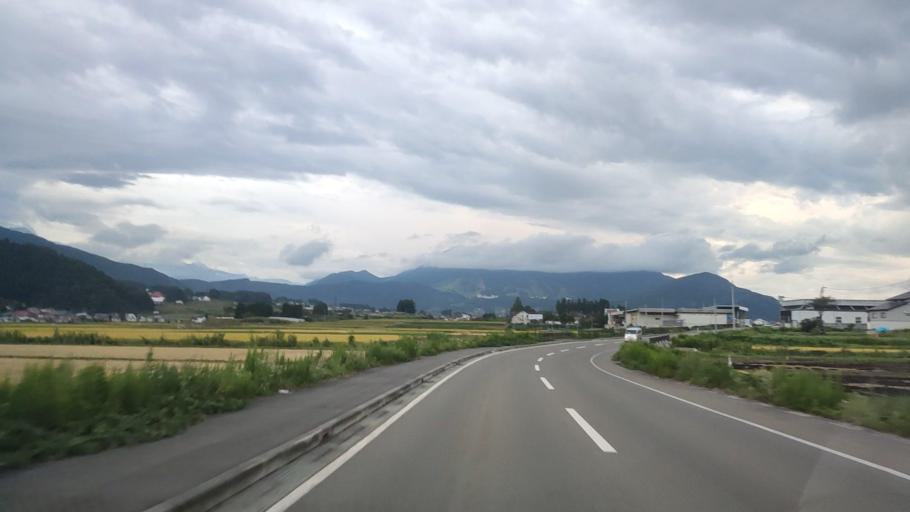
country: JP
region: Nagano
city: Iiyama
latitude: 36.8760
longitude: 138.4094
